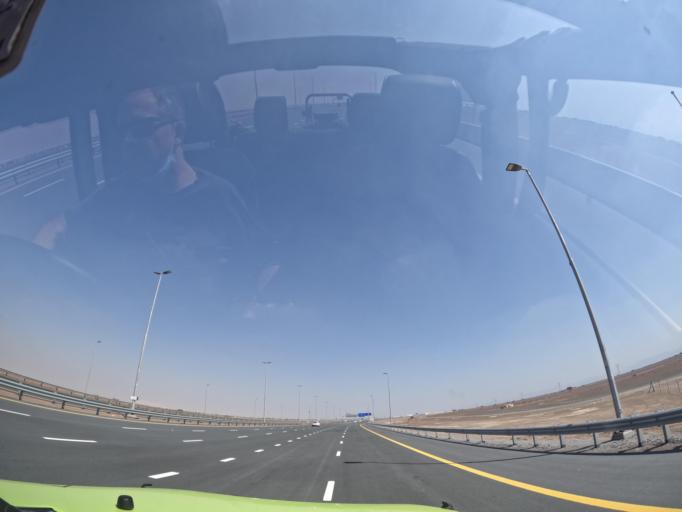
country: AE
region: Ash Shariqah
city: Adh Dhayd
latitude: 24.9196
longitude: 55.8042
